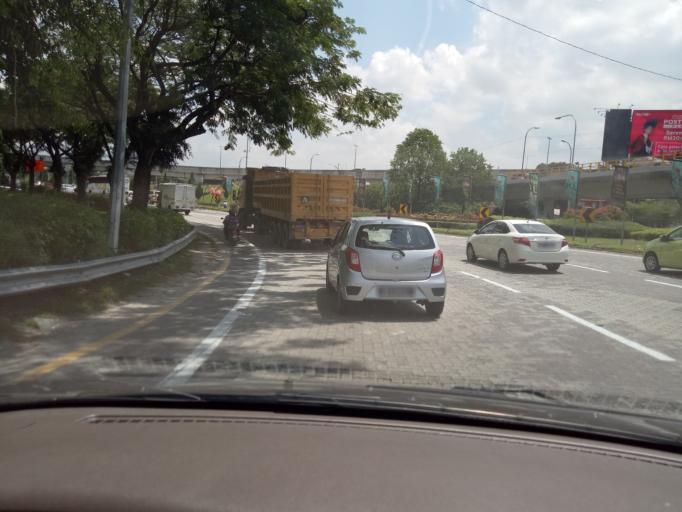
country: MY
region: Kuala Lumpur
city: Kuala Lumpur
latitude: 3.1213
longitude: 101.7080
